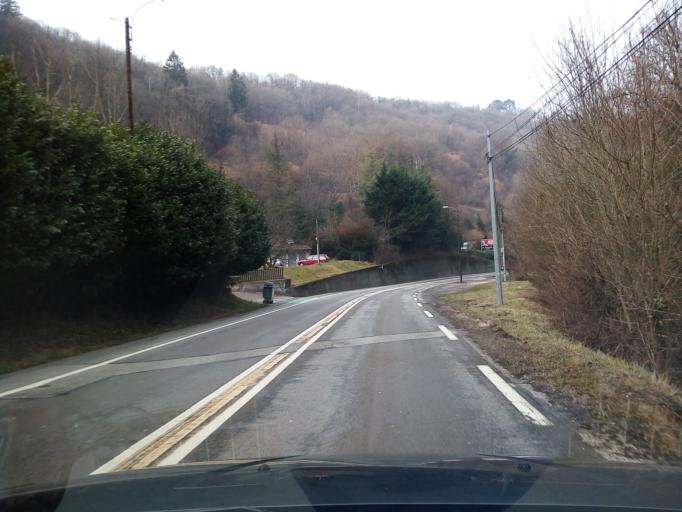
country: FR
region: Rhone-Alpes
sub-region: Departement de l'Isere
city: Gieres
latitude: 45.1696
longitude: 5.7919
